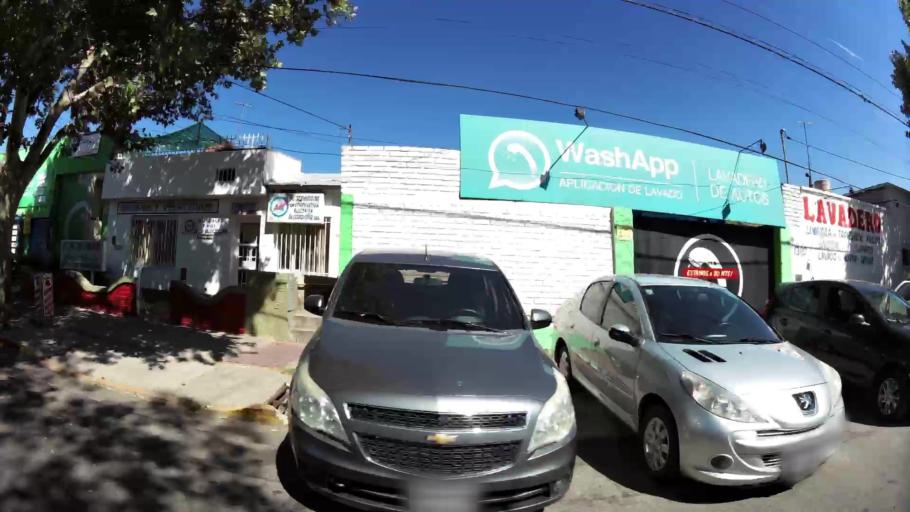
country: AR
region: Mendoza
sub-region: Departamento de Godoy Cruz
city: Godoy Cruz
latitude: -32.9119
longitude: -68.8601
